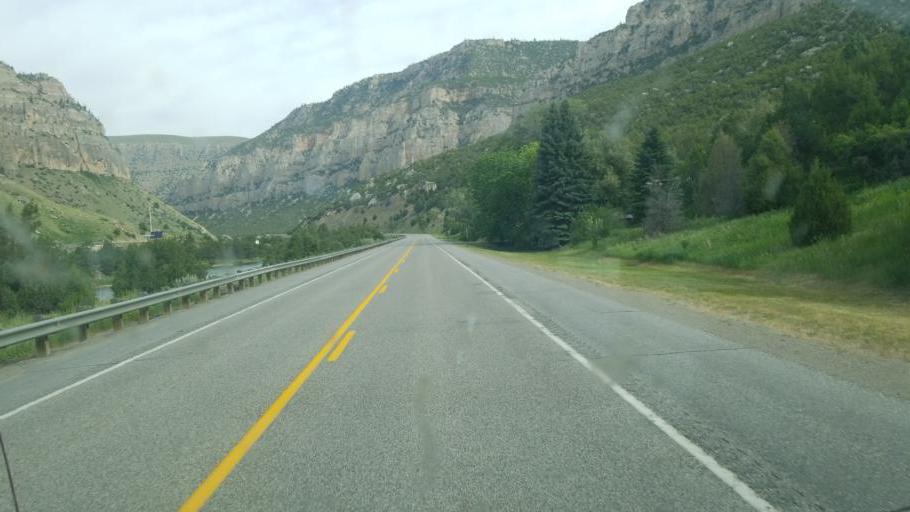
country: US
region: Wyoming
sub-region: Hot Springs County
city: Thermopolis
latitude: 43.4977
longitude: -108.1590
